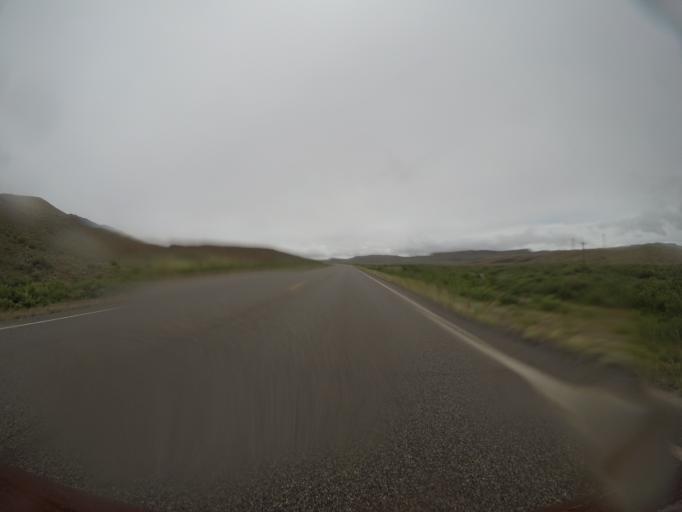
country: US
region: Wyoming
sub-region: Big Horn County
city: Lovell
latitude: 44.9558
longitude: -108.2926
